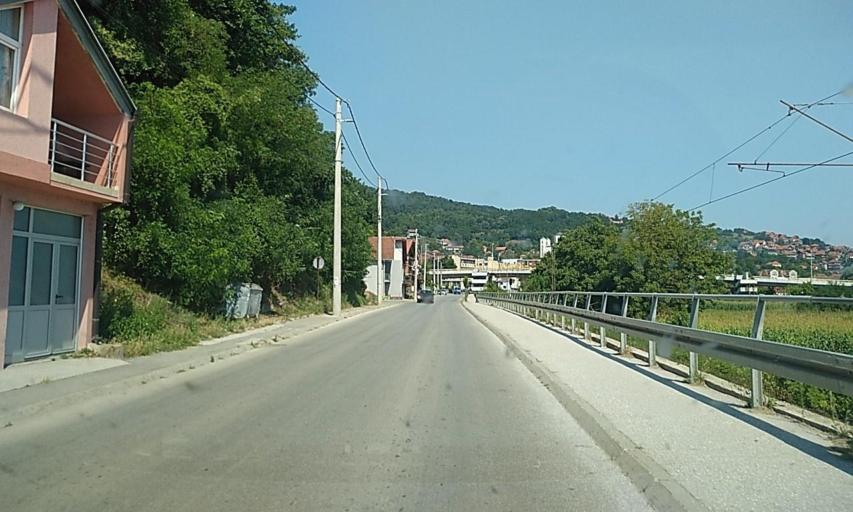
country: RS
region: Central Serbia
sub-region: Pcinjski Okrug
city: Vladicin Han
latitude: 42.7037
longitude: 22.0606
